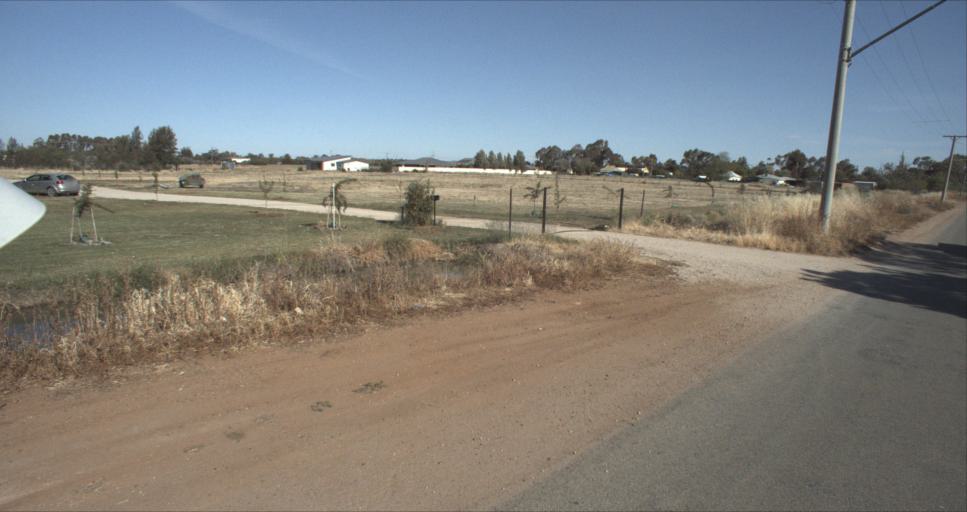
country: AU
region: New South Wales
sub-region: Leeton
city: Leeton
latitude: -34.5475
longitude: 146.4144
